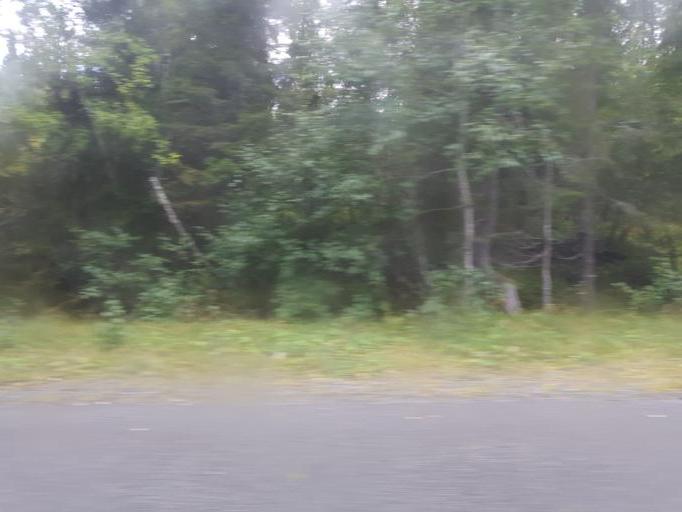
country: NO
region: Sor-Trondelag
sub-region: Trondheim
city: Trondheim
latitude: 63.4155
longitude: 10.2965
